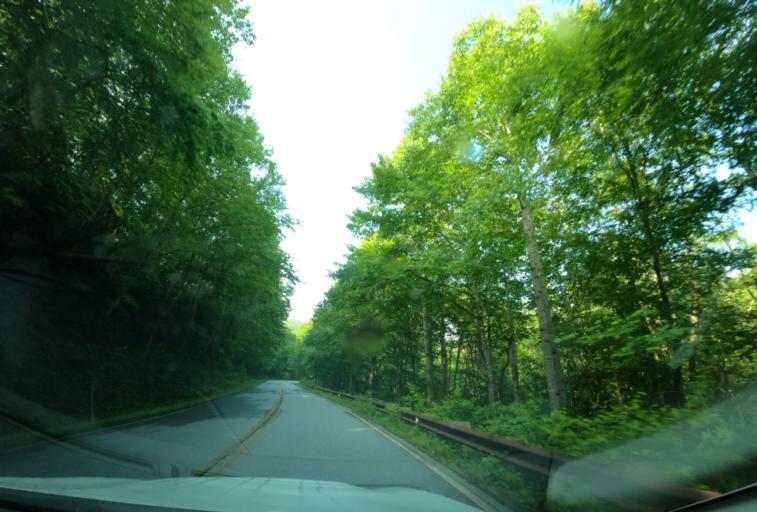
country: US
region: North Carolina
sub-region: Transylvania County
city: Brevard
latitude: 35.2583
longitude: -82.9115
